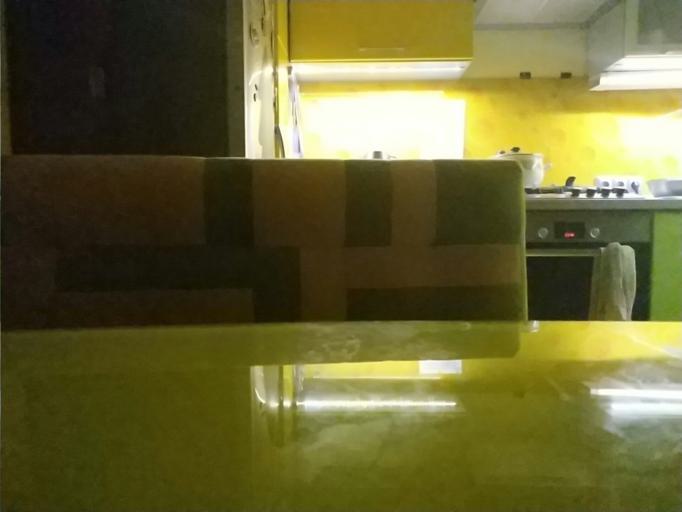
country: RU
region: Republic of Karelia
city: Pyaozerskiy
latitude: 65.7167
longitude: 30.5111
